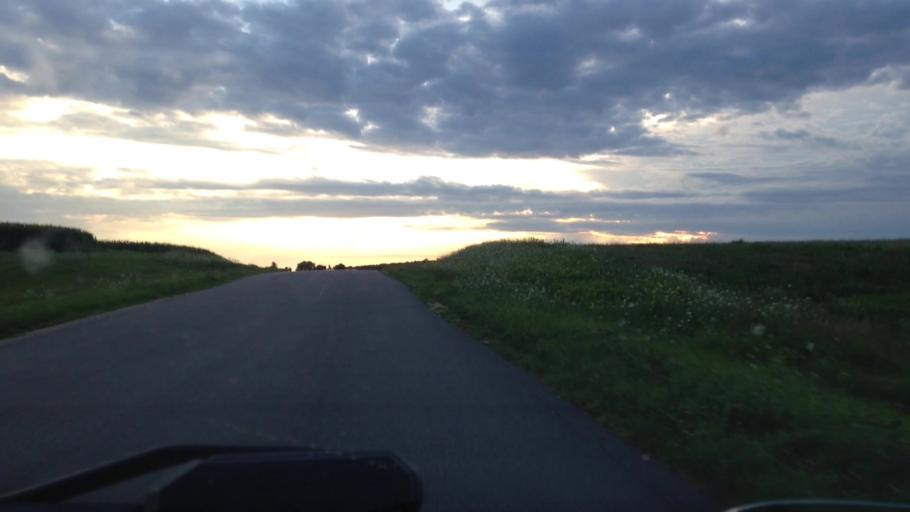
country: US
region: Wisconsin
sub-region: Dodge County
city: Theresa
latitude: 43.4861
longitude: -88.4816
